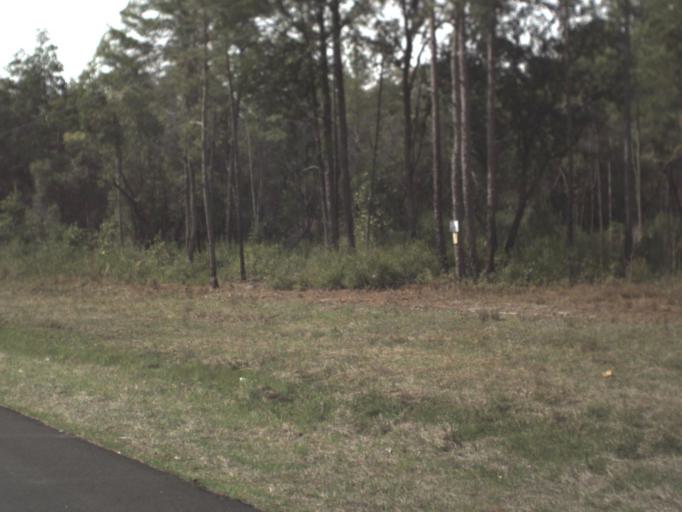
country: US
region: Florida
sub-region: Gadsden County
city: Midway
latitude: 30.4374
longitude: -84.4995
